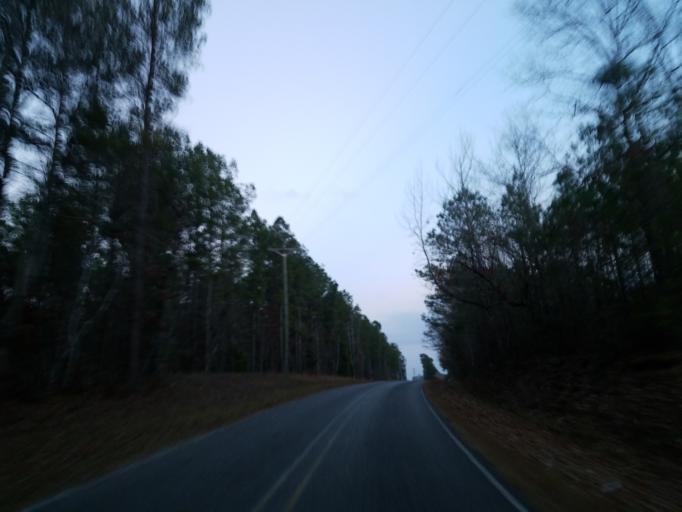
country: US
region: Alabama
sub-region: Sumter County
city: York
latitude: 32.4064
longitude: -88.4550
